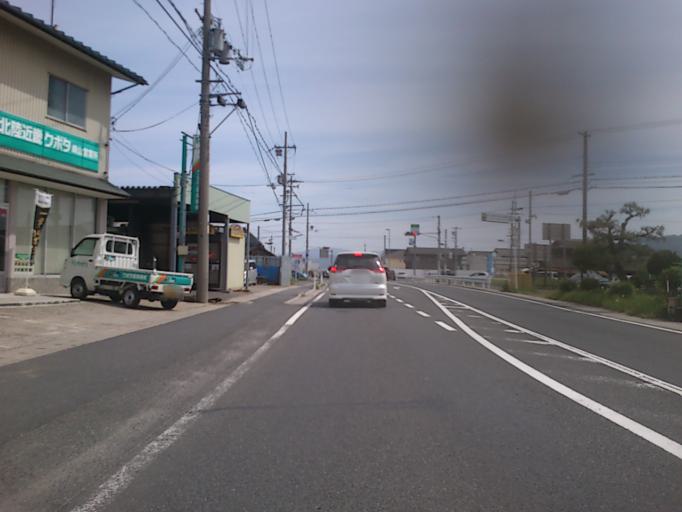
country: JP
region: Kyoto
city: Miyazu
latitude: 35.6204
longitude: 135.0746
